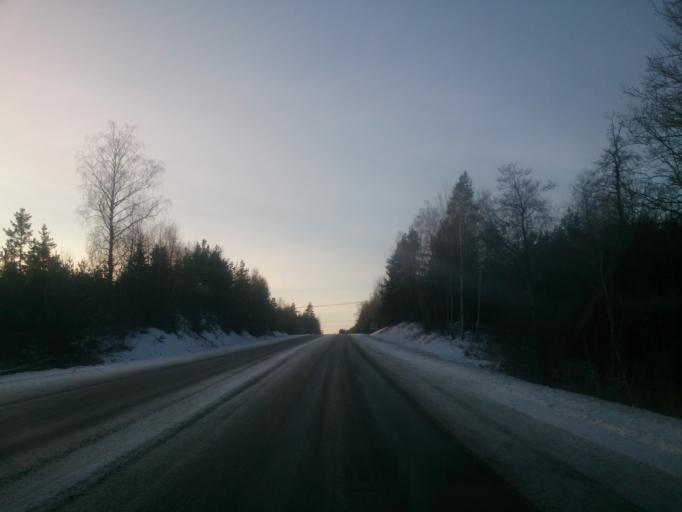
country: SE
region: OEstergoetland
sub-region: Norrkopings Kommun
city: Kimstad
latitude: 58.5204
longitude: 15.9974
